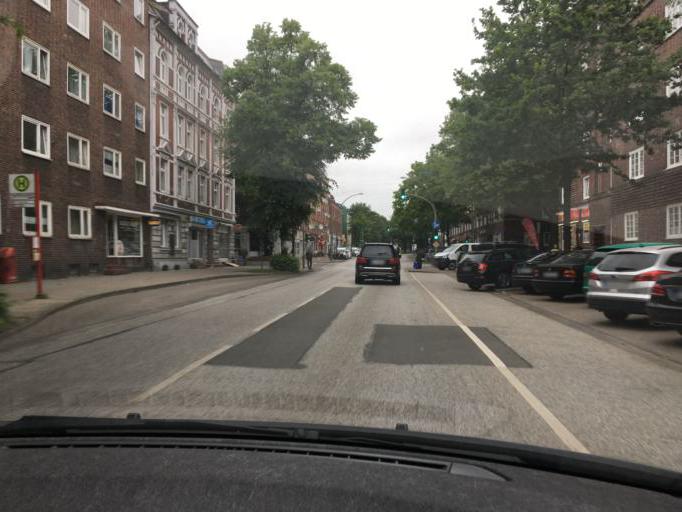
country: DE
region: Hamburg
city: Kleiner Grasbrook
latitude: 53.5148
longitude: 9.9933
